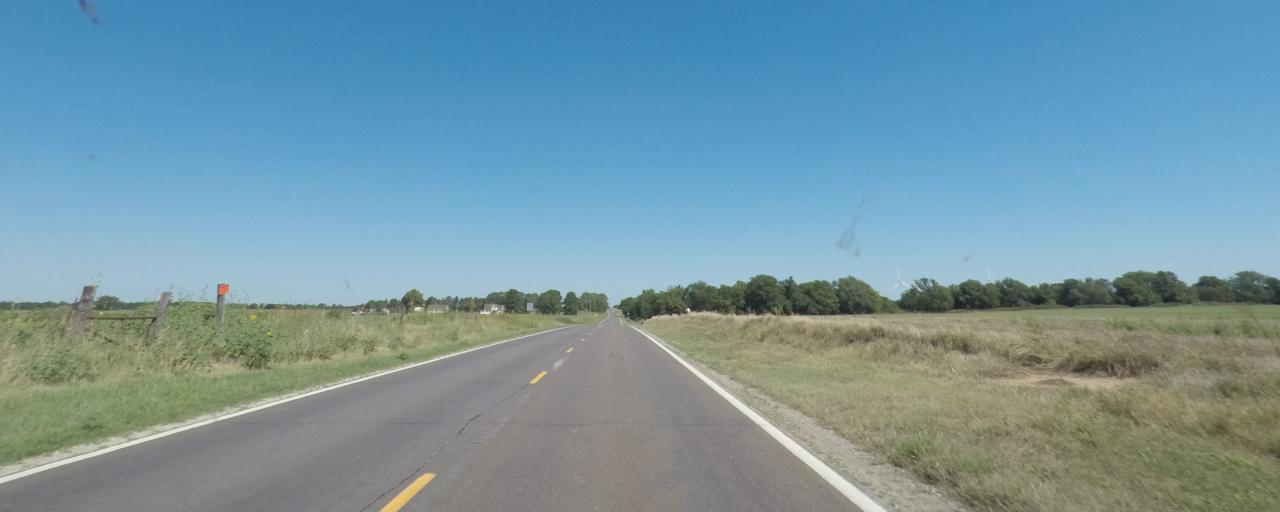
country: US
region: Kansas
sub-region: Sumner County
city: Wellington
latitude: 37.1243
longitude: -97.4017
